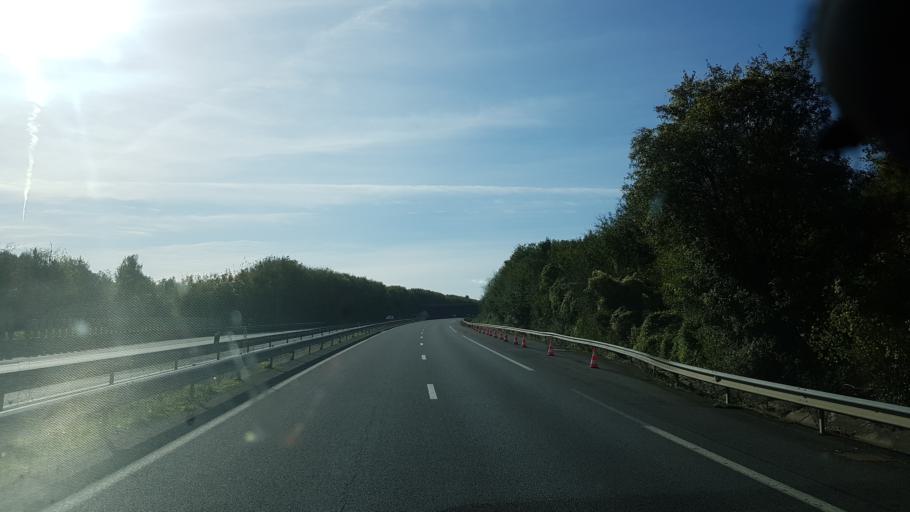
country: FR
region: Poitou-Charentes
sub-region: Departement de la Charente
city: Mornac
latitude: 45.7113
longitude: 0.2915
